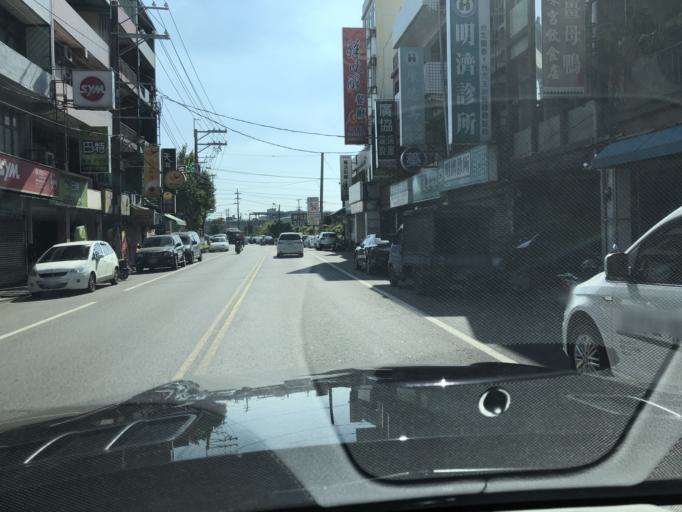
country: TW
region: Taiwan
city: Taoyuan City
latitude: 25.0844
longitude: 121.2861
